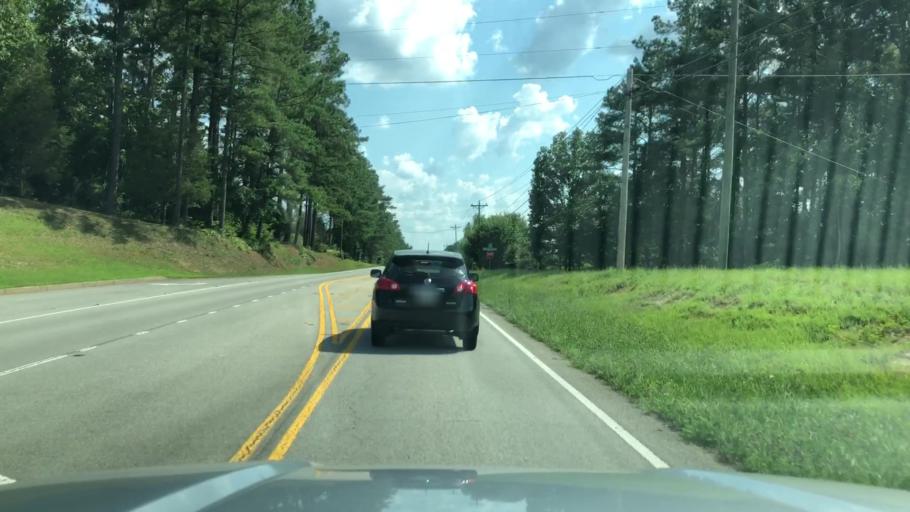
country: US
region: Georgia
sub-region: Paulding County
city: Dallas
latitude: 33.9675
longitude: -84.8253
